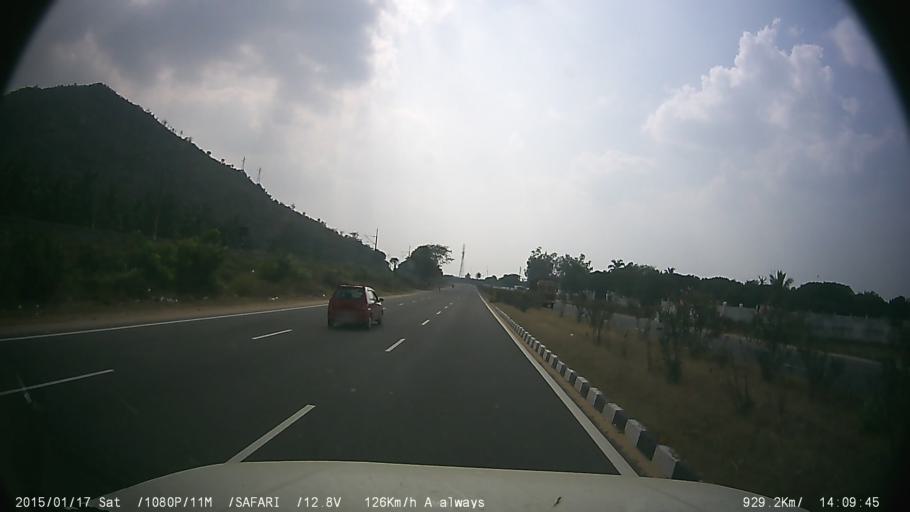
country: IN
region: Tamil Nadu
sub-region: Vellore
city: Ambur
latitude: 12.8143
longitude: 78.7457
